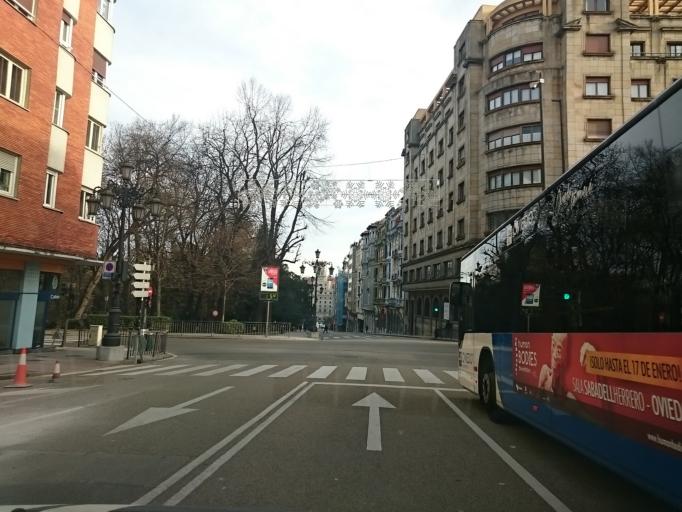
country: ES
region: Asturias
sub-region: Province of Asturias
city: Oviedo
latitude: 43.3628
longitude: -5.8472
